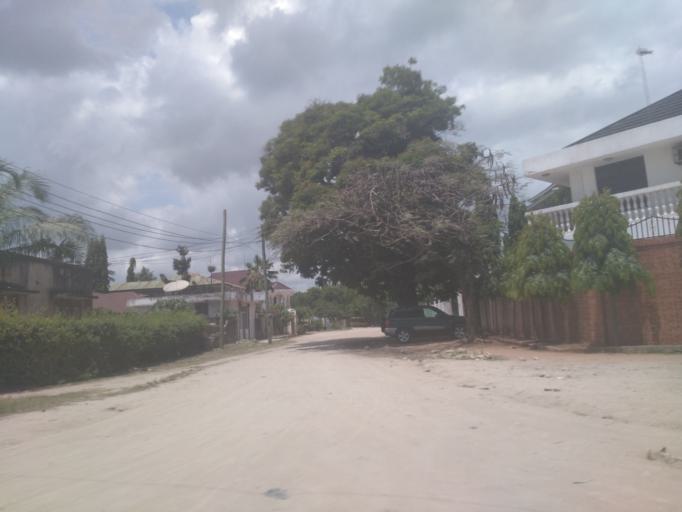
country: TZ
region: Dar es Salaam
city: Dar es Salaam
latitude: -6.8457
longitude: 39.2702
